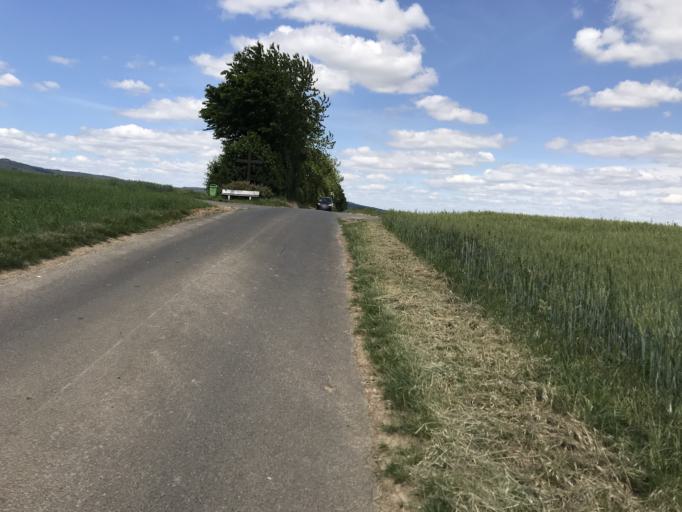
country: DE
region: Hesse
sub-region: Regierungsbezirk Darmstadt
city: Ober-Morlen
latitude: 50.3878
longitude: 8.6864
